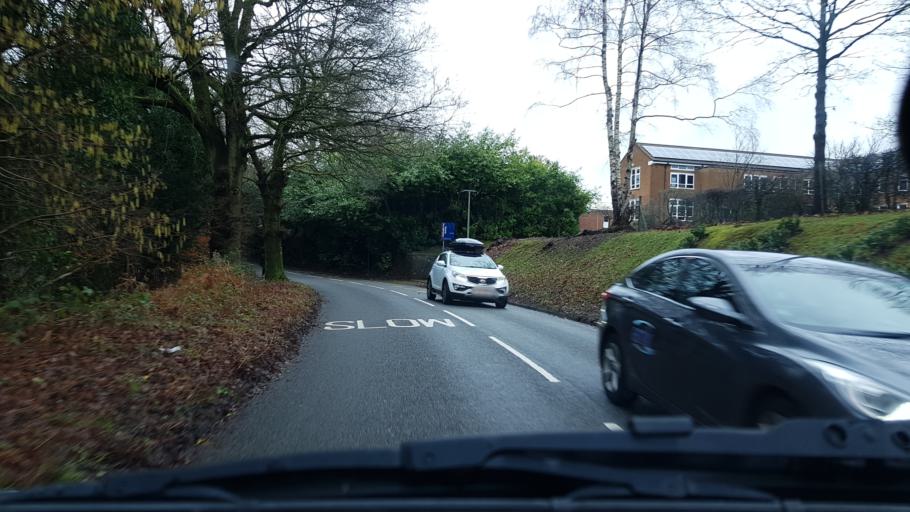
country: GB
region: England
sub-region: Surrey
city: Hindhead
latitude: 51.0922
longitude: -0.7495
